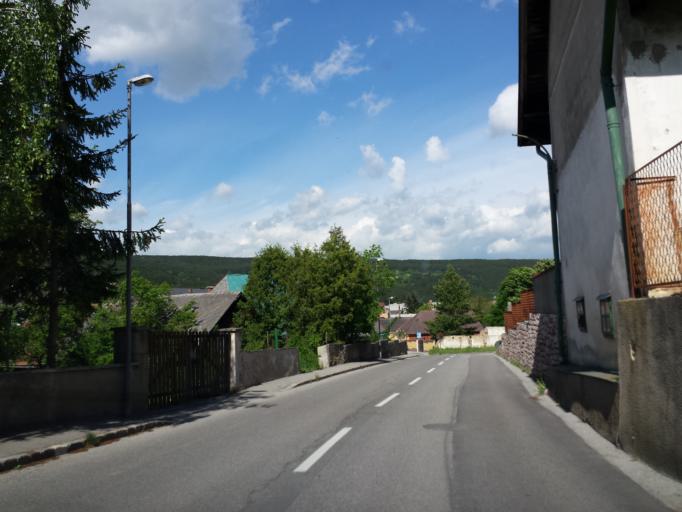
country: AT
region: Lower Austria
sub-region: Politischer Bezirk Wiener Neustadt
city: Markt Piesting
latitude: 47.8711
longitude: 16.1241
